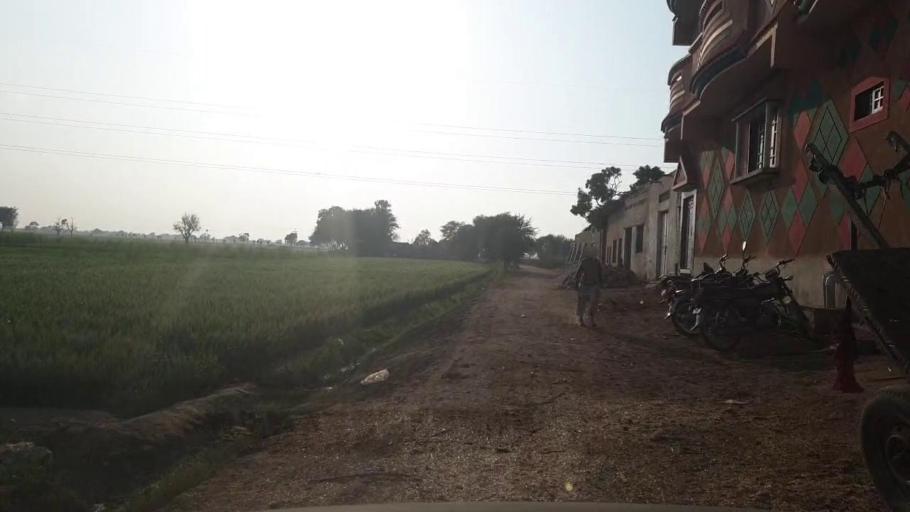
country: PK
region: Sindh
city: Hala
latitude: 25.8462
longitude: 68.4164
